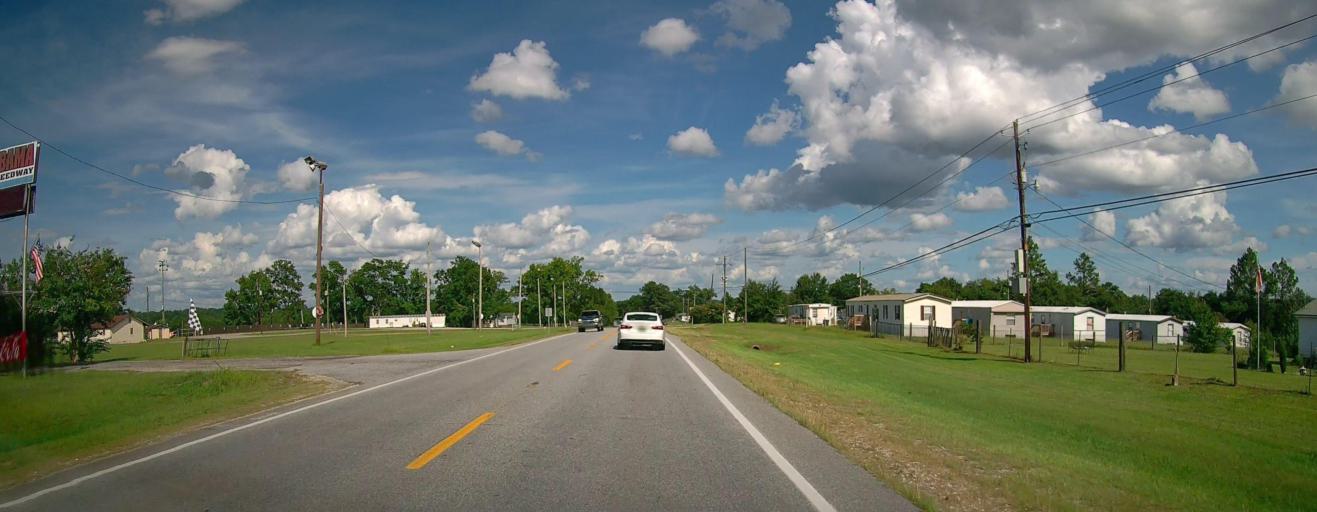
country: US
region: Alabama
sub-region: Russell County
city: Ladonia
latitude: 32.4611
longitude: -85.1504
